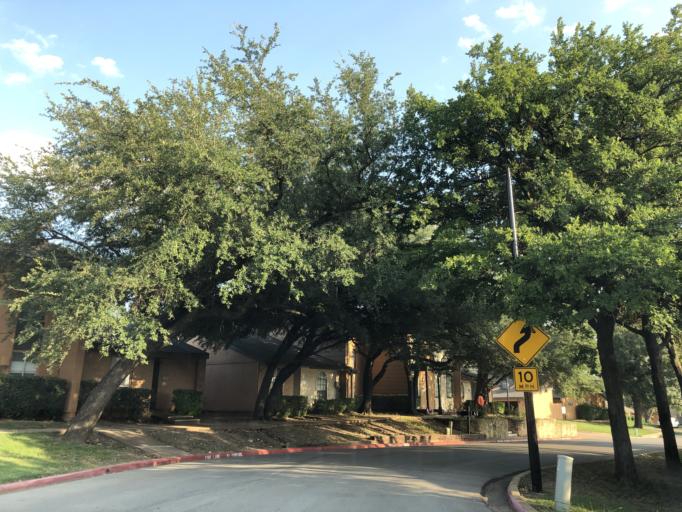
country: US
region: Texas
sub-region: Dallas County
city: Sunnyvale
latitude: 32.8441
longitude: -96.5891
